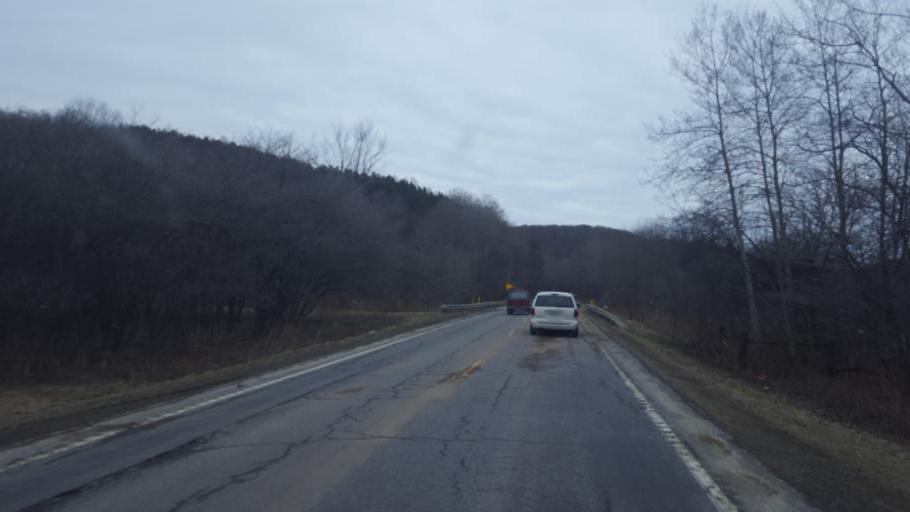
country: US
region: Pennsylvania
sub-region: Potter County
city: Coudersport
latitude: 41.8354
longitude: -77.9265
